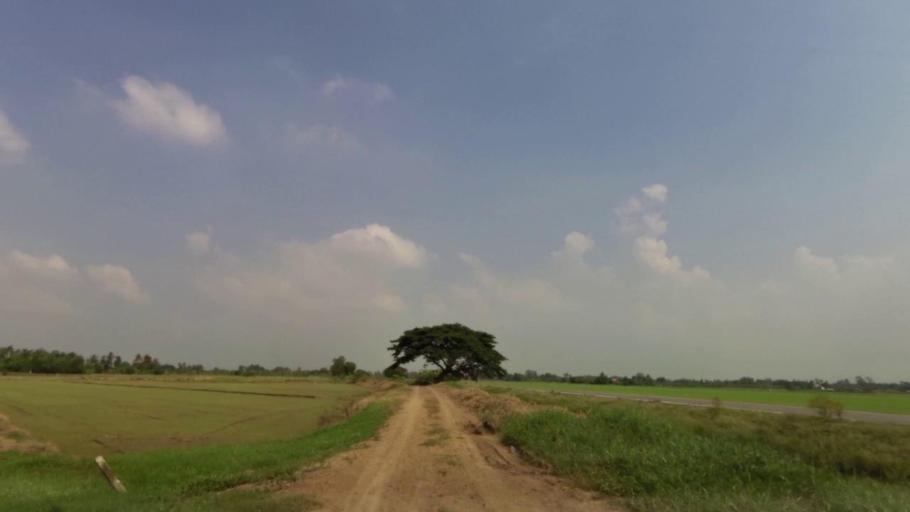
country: TH
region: Ang Thong
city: Pho Thong
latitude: 14.6224
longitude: 100.4038
